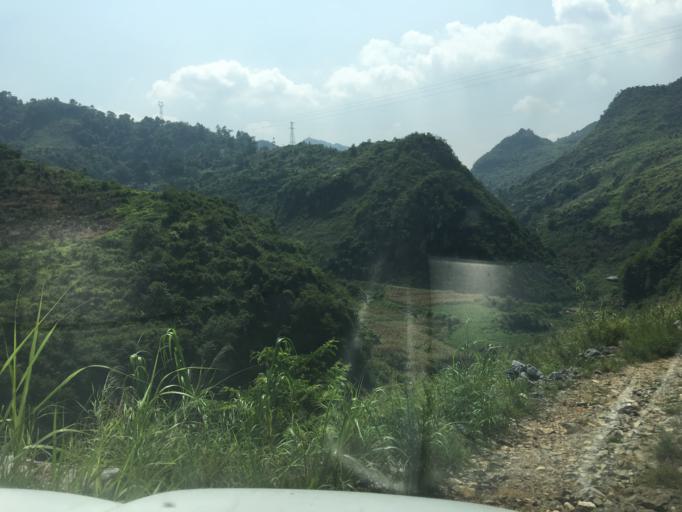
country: CN
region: Guangxi Zhuangzu Zizhiqu
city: Xinzhou
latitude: 24.9933
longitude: 105.7466
